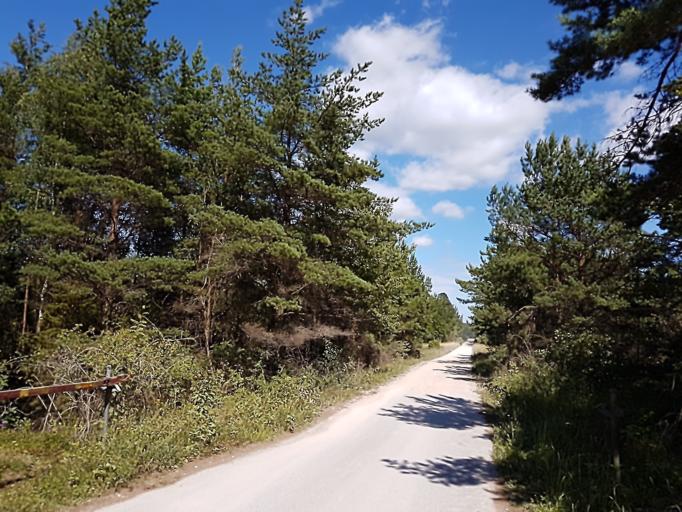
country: SE
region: Gotland
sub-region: Gotland
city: Visby
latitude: 57.6050
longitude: 18.3511
